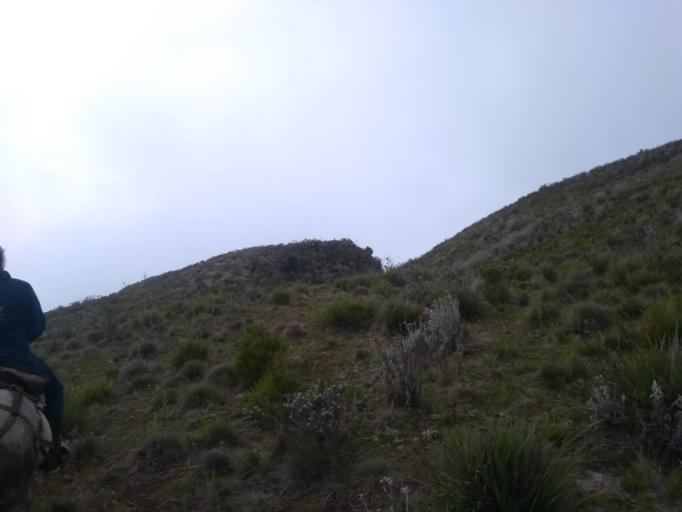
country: CO
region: Cesar
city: Manaure Balcon del Cesar
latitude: 10.2093
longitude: -73.0088
